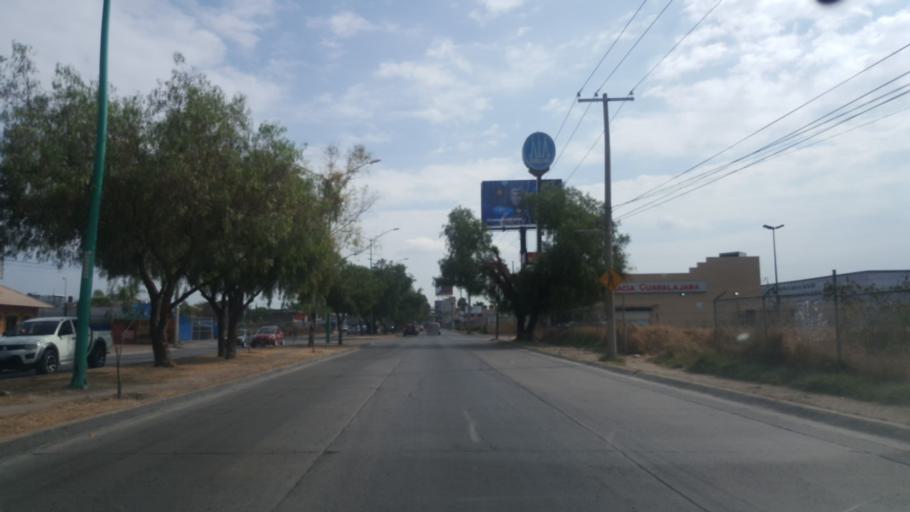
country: MX
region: Guanajuato
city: Leon
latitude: 21.1050
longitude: -101.6508
